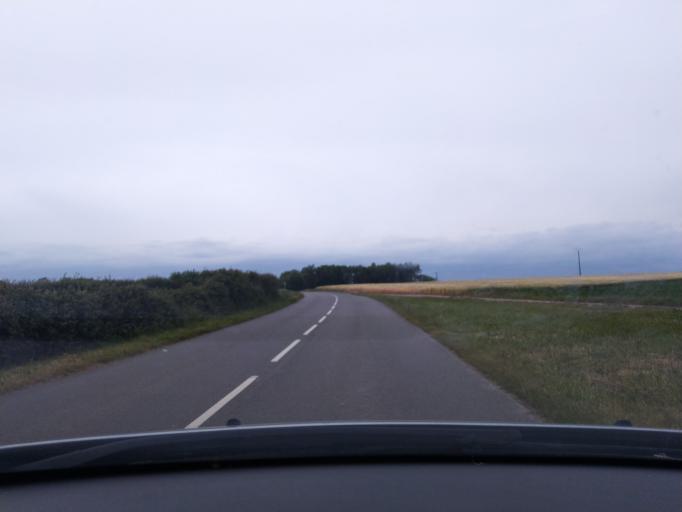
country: FR
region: Nord-Pas-de-Calais
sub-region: Departement du Pas-de-Calais
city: Wissant
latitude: 50.8469
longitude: 1.6793
